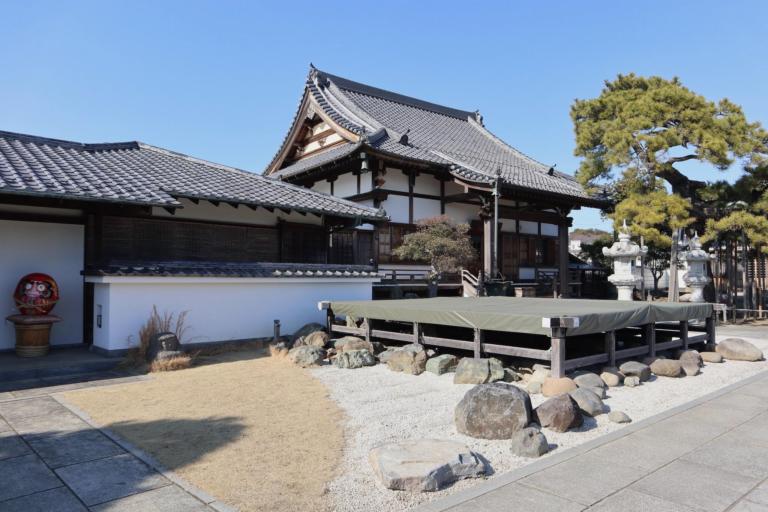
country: JP
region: Chiba
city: Matsudo
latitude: 35.7794
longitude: 139.8711
